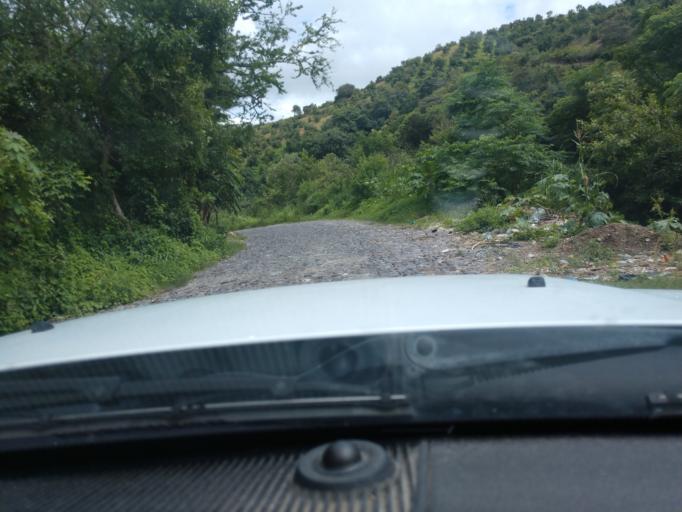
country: MX
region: Nayarit
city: Xalisco
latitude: 21.4417
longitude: -104.9107
